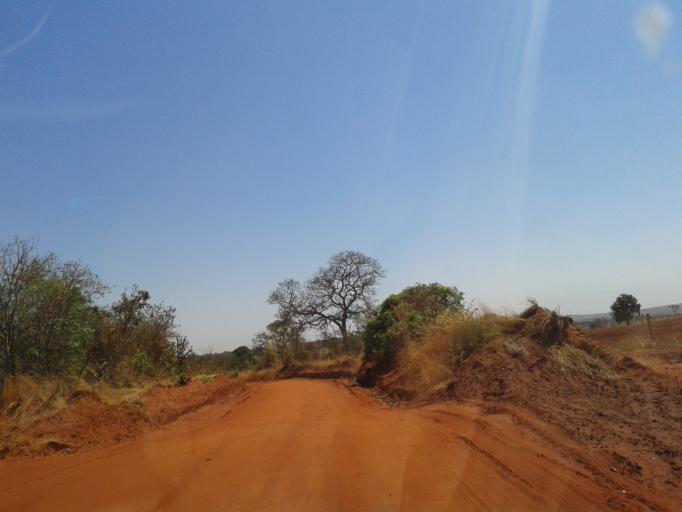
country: BR
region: Minas Gerais
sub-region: Ituiutaba
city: Ituiutaba
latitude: -19.0078
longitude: -49.3636
